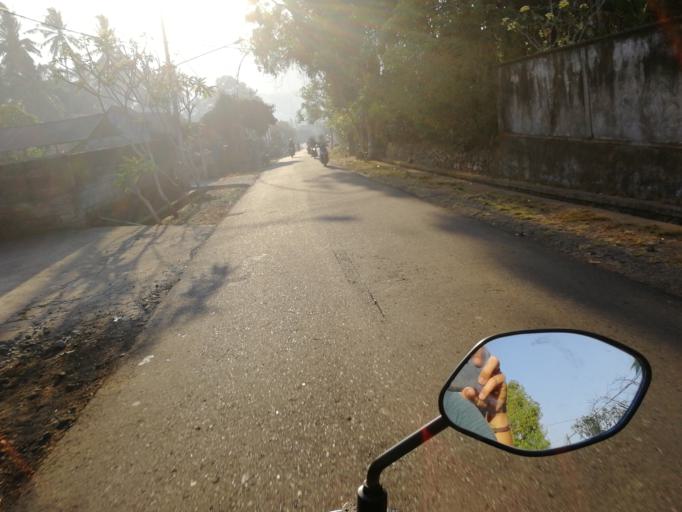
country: ID
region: Bali
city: Tistagede
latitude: -8.3859
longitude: 115.6103
